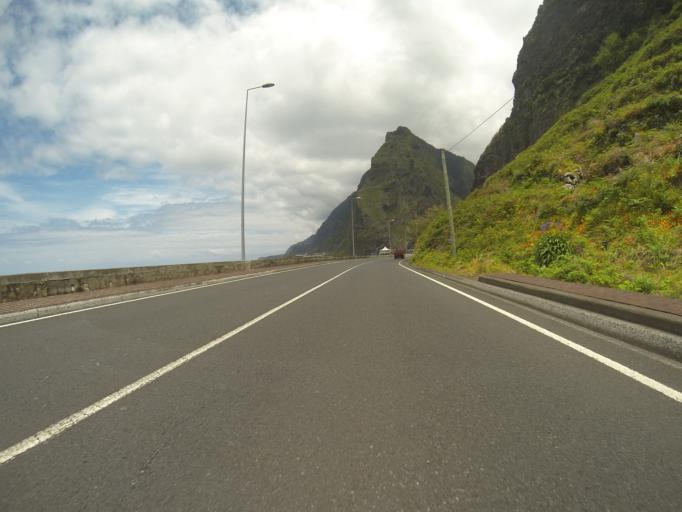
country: PT
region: Madeira
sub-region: Sao Vicente
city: Sao Vicente
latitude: 32.8083
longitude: -17.0564
